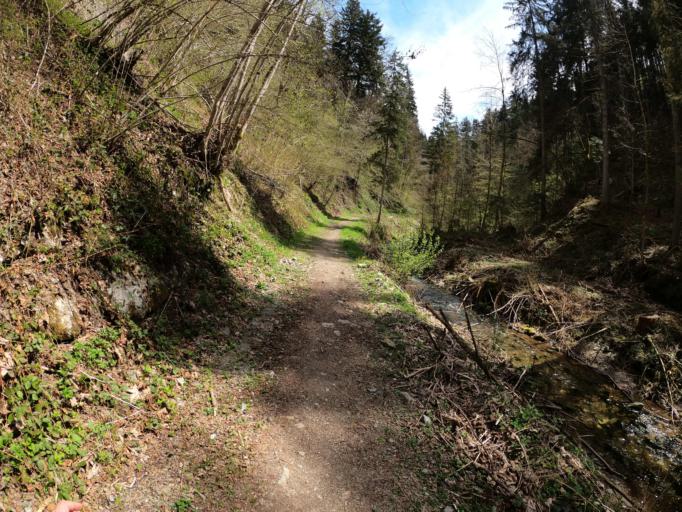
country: AT
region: Salzburg
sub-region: Politischer Bezirk Sankt Johann im Pongau
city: Pfarrwerfen
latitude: 47.4627
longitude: 13.2112
